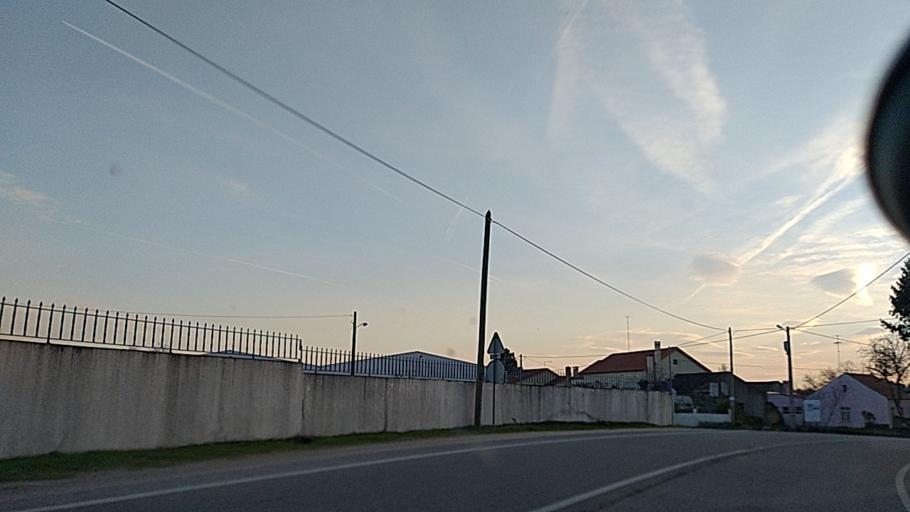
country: PT
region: Guarda
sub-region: Guarda
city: Sequeira
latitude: 40.5838
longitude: -7.1505
